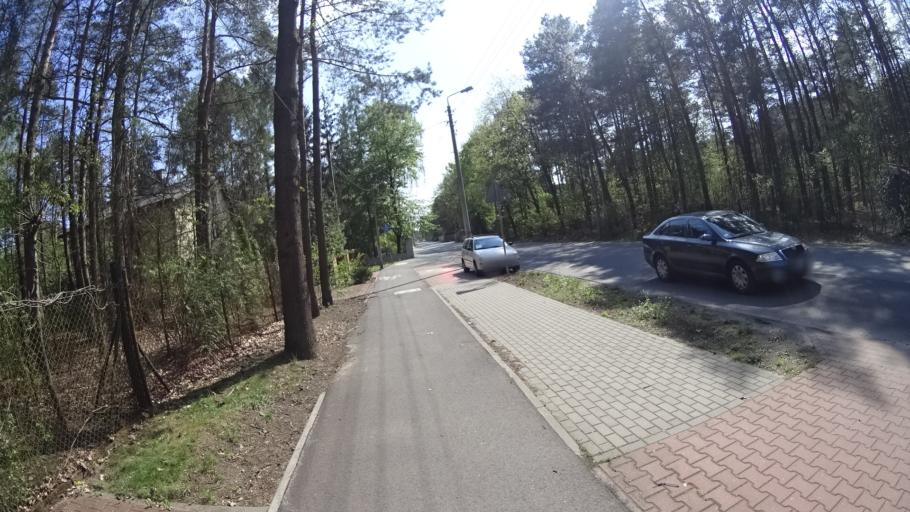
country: PL
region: Masovian Voivodeship
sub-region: Powiat warszawski zachodni
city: Izabelin
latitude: 52.3012
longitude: 20.8075
